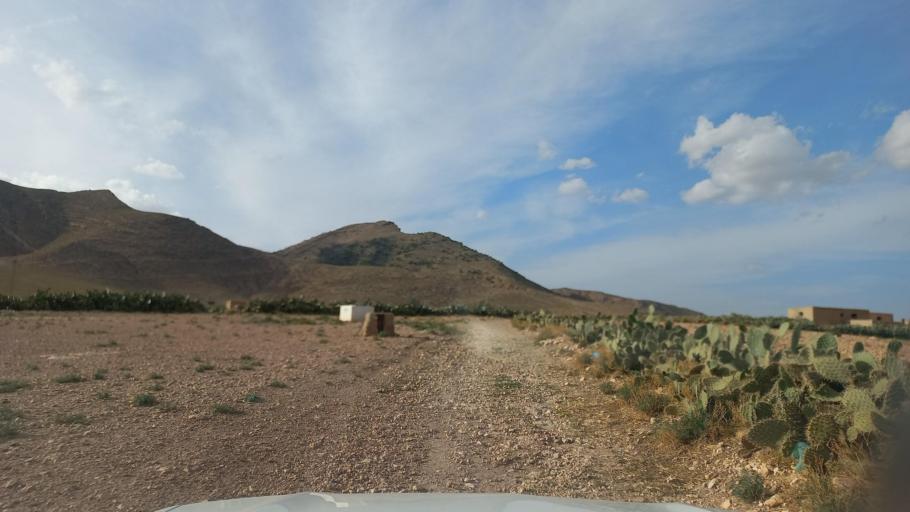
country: TN
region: Al Qasrayn
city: Sbiba
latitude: 35.4573
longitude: 9.0774
